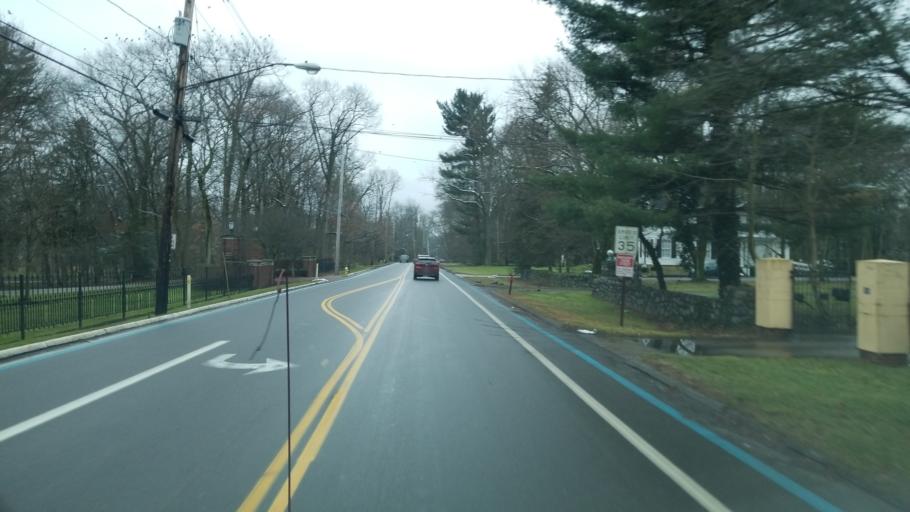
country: US
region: Ohio
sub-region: Summit County
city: Akron
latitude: 41.1161
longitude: -81.5485
